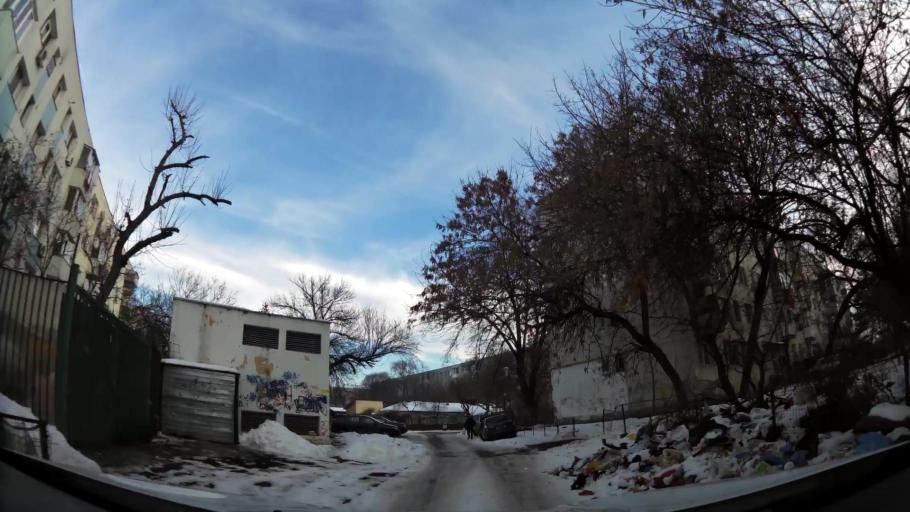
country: RO
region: Bucuresti
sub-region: Municipiul Bucuresti
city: Bucuresti
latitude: 44.3906
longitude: 26.0745
